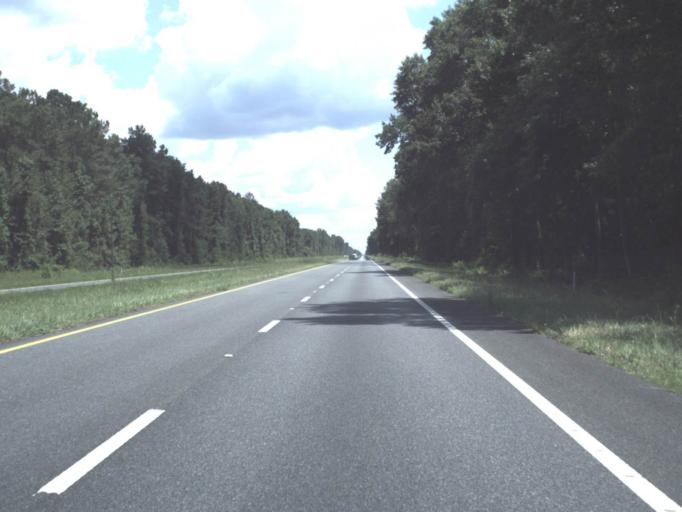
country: US
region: Florida
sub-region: Taylor County
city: Perry
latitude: 30.2940
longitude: -83.7398
